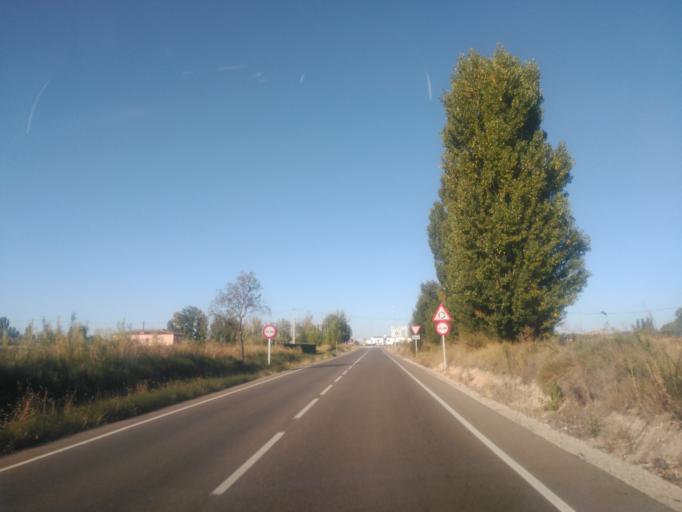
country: ES
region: Castille and Leon
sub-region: Provincia de Burgos
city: Fresnillo de las Duenas
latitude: 41.6761
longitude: -3.6562
